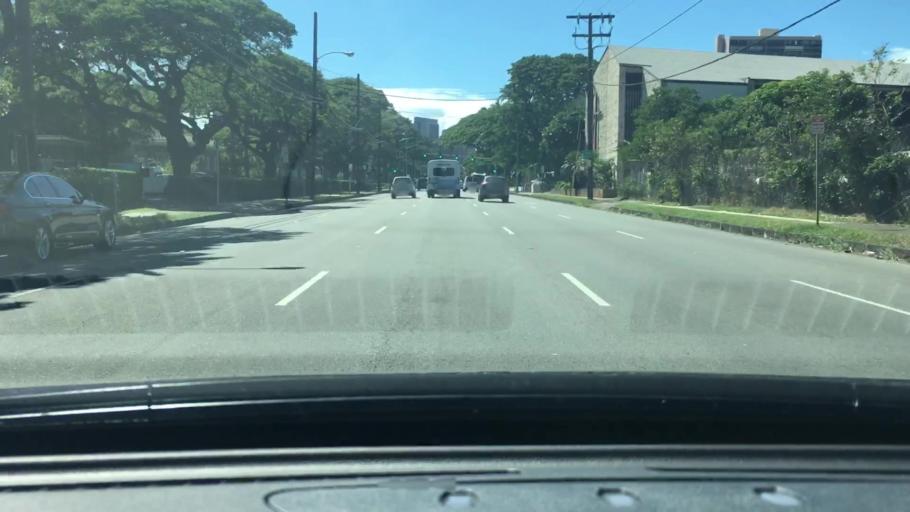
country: US
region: Hawaii
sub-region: Honolulu County
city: Honolulu
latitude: 21.3028
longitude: -157.8467
